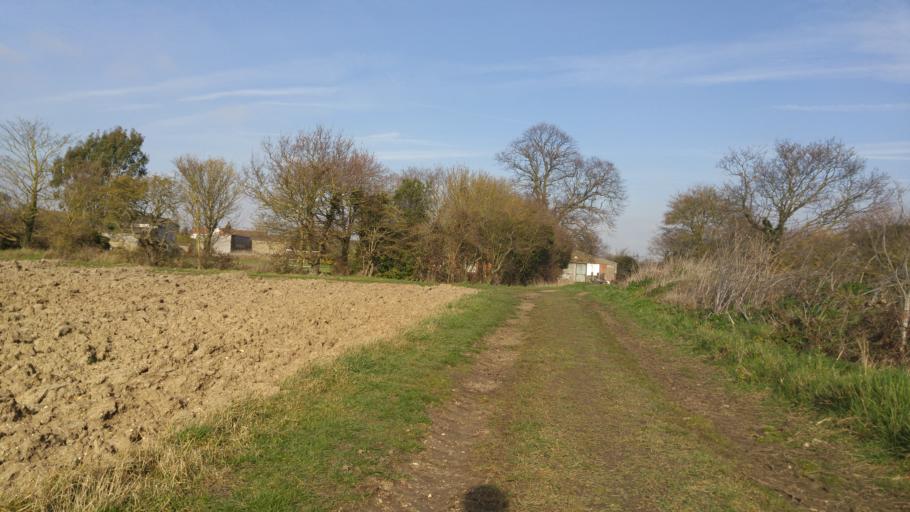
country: GB
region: England
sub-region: Essex
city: Little Clacton
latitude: 51.8245
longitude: 1.1712
